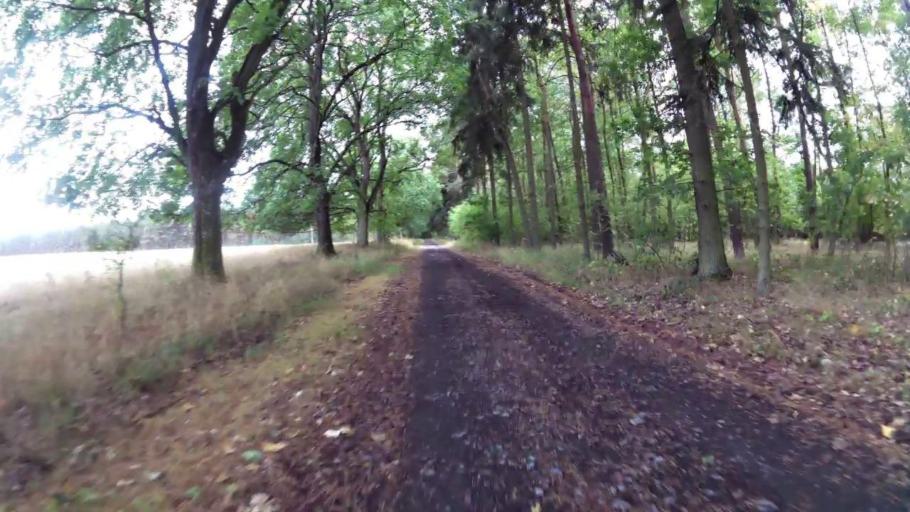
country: PL
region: West Pomeranian Voivodeship
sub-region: Powiat mysliborski
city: Debno
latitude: 52.8688
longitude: 14.7140
